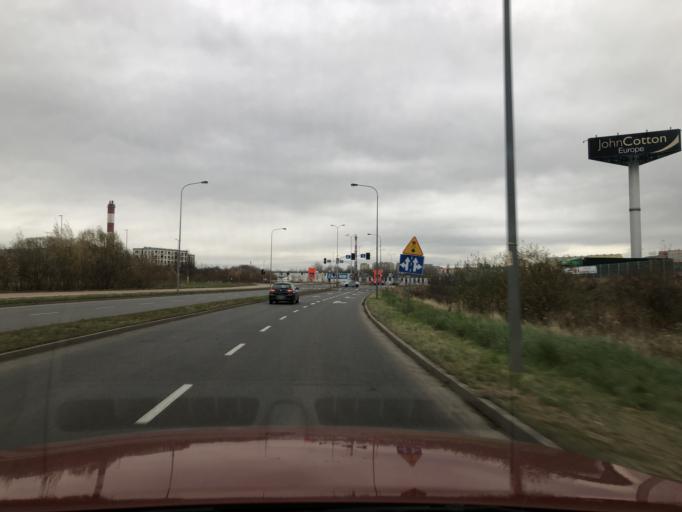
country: PL
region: Lower Silesian Voivodeship
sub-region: Powiat walbrzyski
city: Szczawno-Zdroj
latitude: 50.8180
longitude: 16.2677
